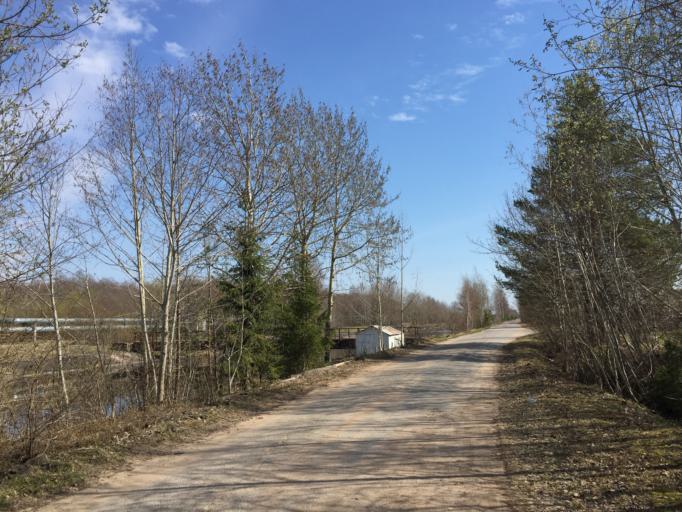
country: EE
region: Ida-Virumaa
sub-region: Narva linn
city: Narva
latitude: 59.3522
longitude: 28.1517
